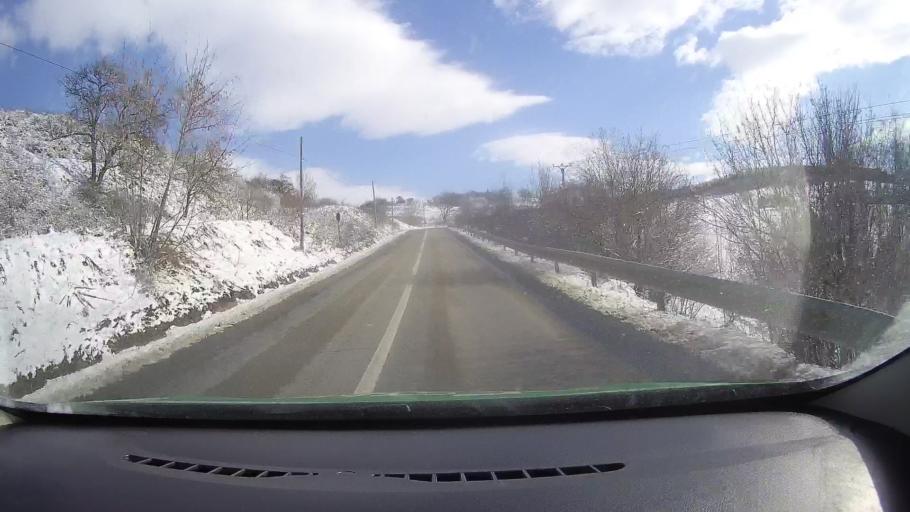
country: RO
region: Sibiu
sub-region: Comuna Barghis
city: Barghis
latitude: 45.9826
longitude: 24.5092
